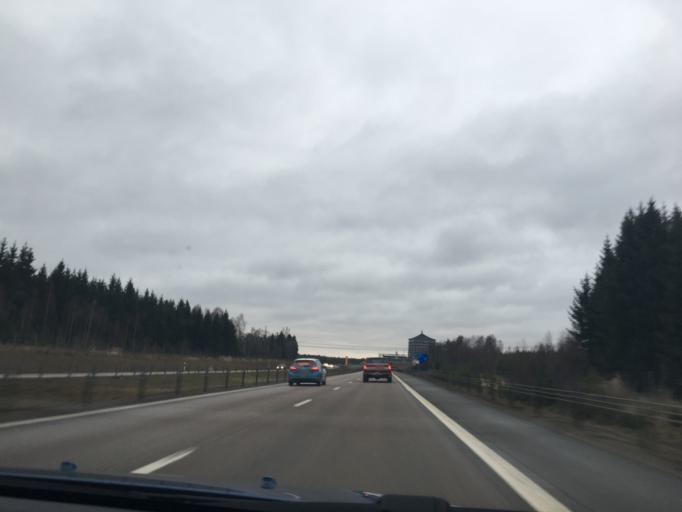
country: SE
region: Uppsala
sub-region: Alvkarleby Kommun
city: AElvkarleby
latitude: 60.4557
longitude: 17.4153
